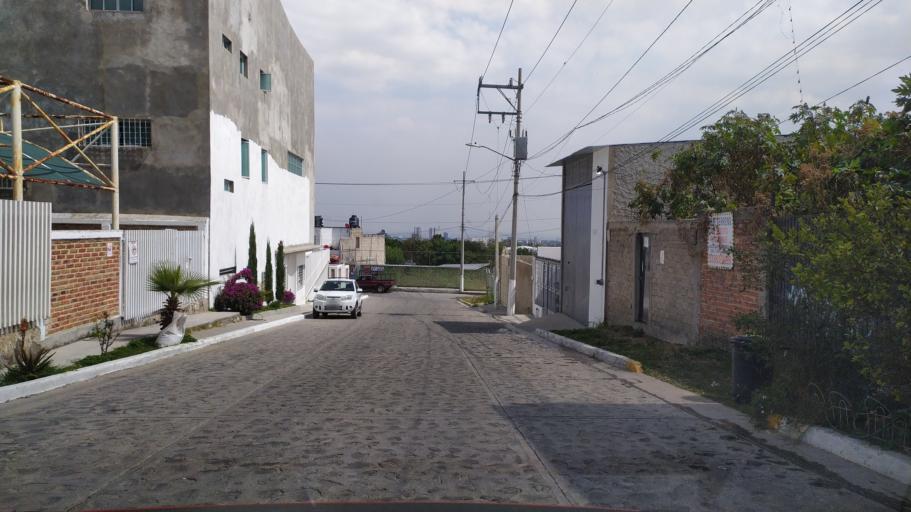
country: MX
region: Jalisco
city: Guadalajara
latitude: 20.6610
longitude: -103.4537
